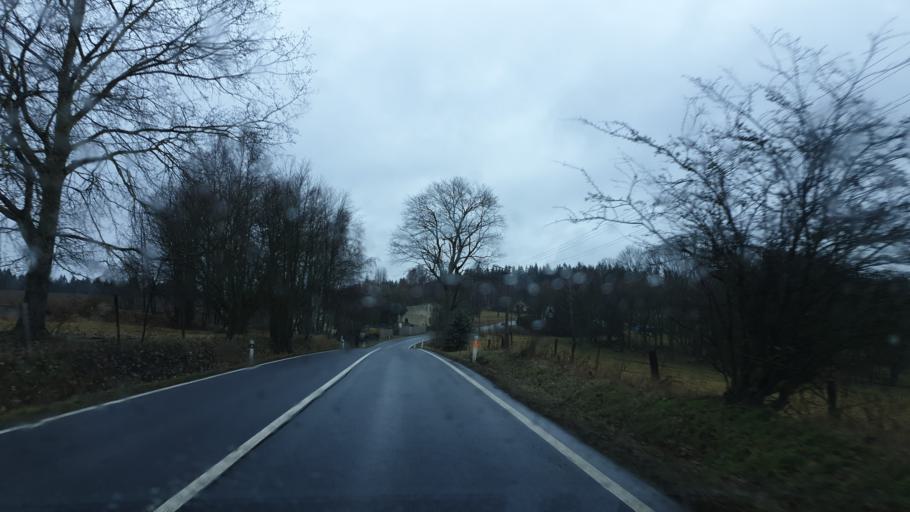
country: CZ
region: Karlovarsky
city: As
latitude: 50.2546
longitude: 12.1782
